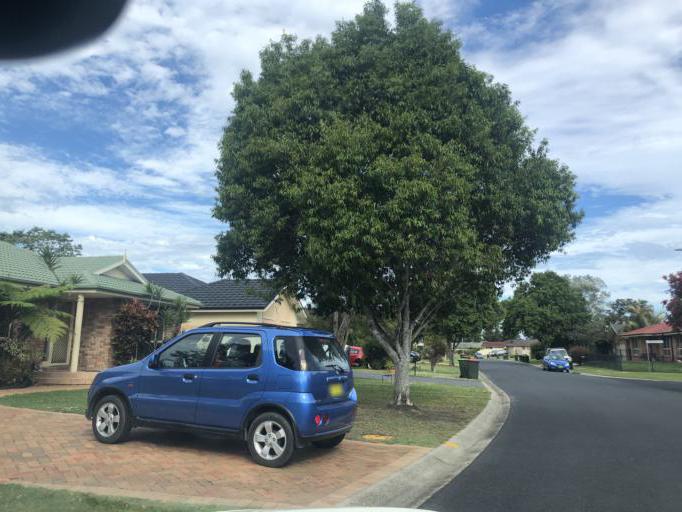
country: AU
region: New South Wales
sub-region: Coffs Harbour
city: Coffs Harbour
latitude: -30.2870
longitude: 153.0986
